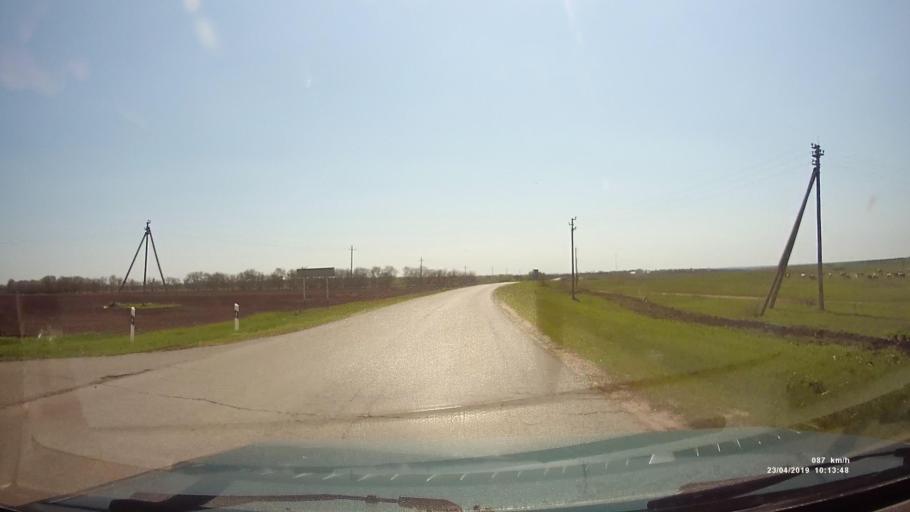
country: RU
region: Rostov
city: Sovetskoye
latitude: 46.6828
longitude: 42.3620
